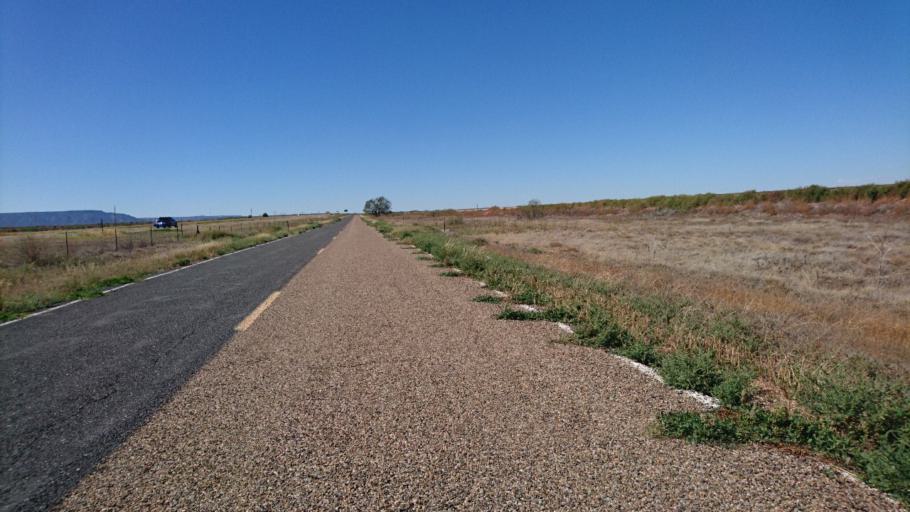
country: US
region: New Mexico
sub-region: Quay County
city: Tucumcari
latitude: 35.1026
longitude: -104.0406
